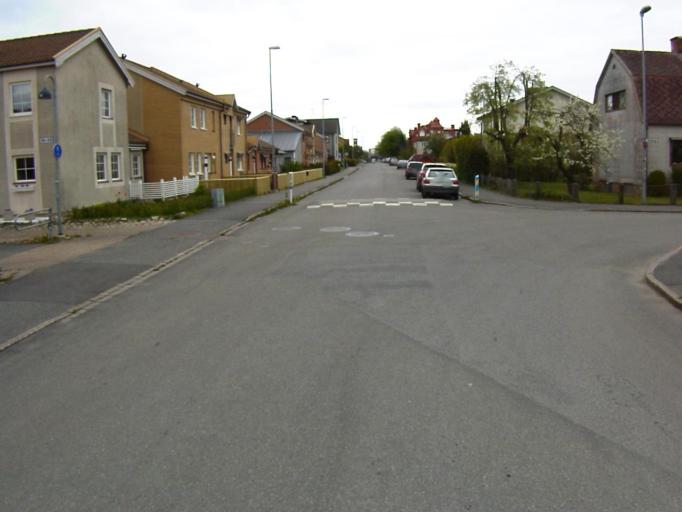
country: SE
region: Skane
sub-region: Kristianstads Kommun
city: Kristianstad
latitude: 56.0189
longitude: 14.1414
